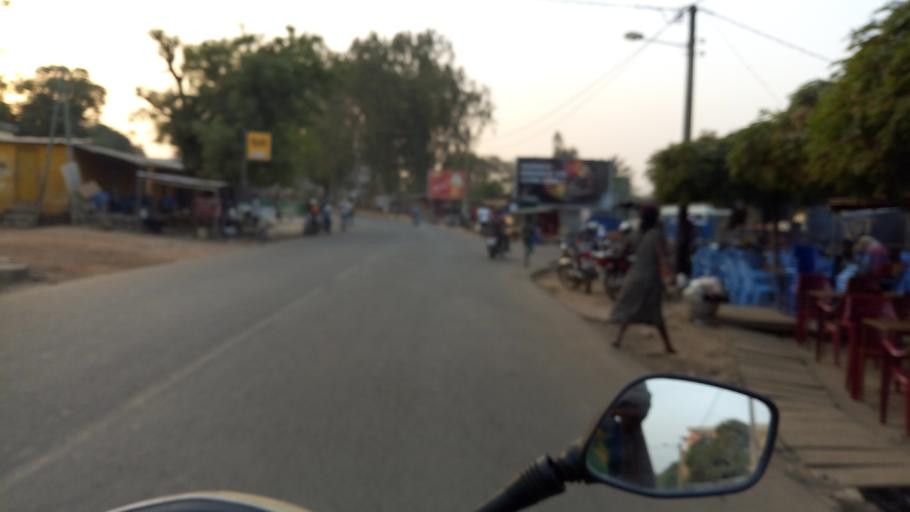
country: TG
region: Kara
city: Kara
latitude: 9.5495
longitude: 1.1849
